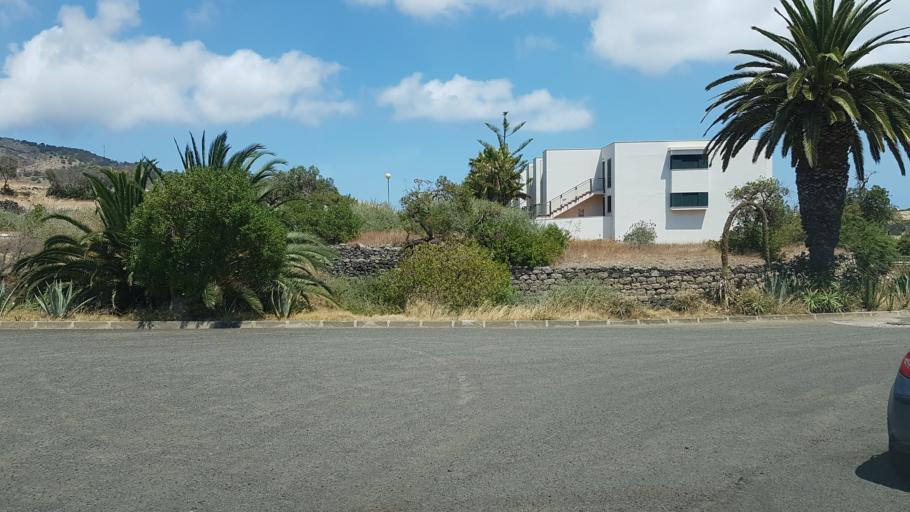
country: PT
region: Madeira
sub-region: Porto Santo
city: Vila de Porto Santo
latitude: 33.0676
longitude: -16.3413
